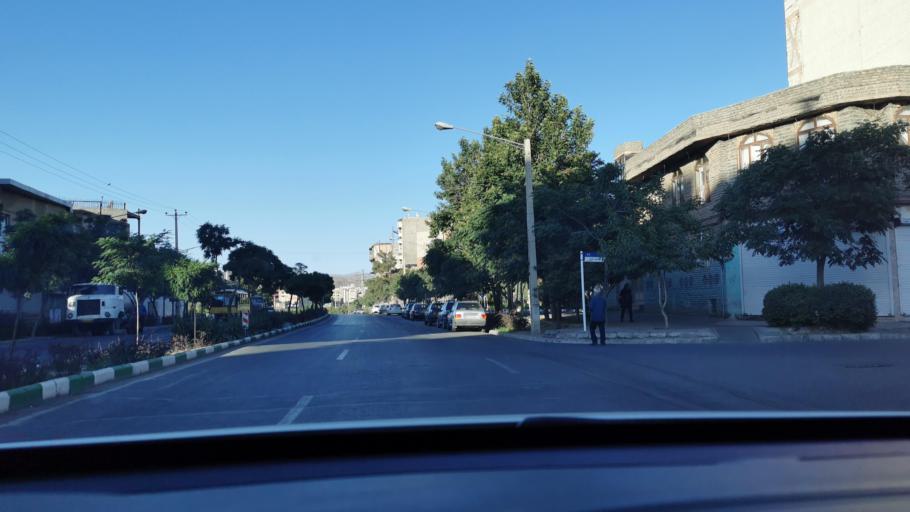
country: IR
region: Razavi Khorasan
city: Mashhad
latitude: 36.3493
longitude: 59.4783
